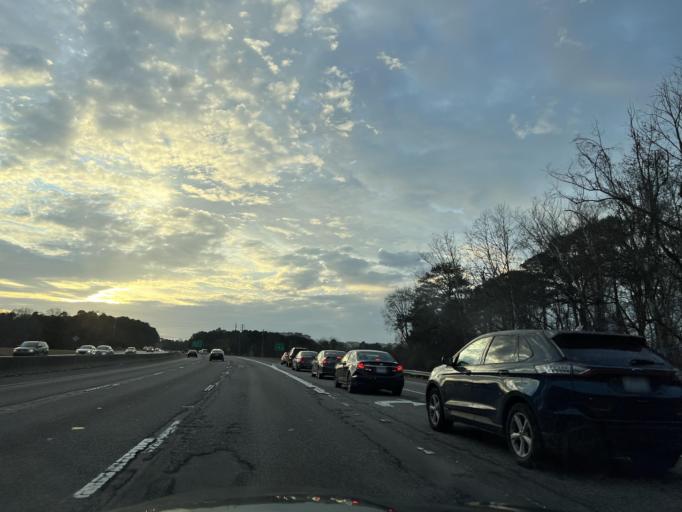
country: US
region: North Carolina
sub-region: Wake County
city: West Raleigh
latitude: 35.8361
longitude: -78.6657
